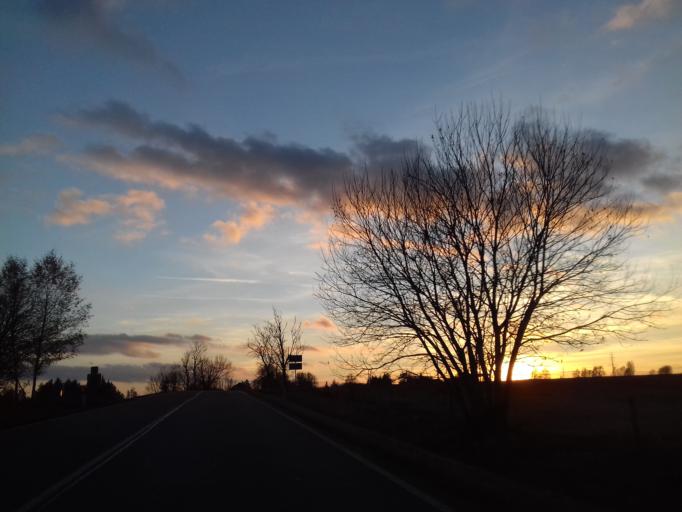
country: CZ
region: Vysocina
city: Krizova
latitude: 49.7134
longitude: 15.8532
